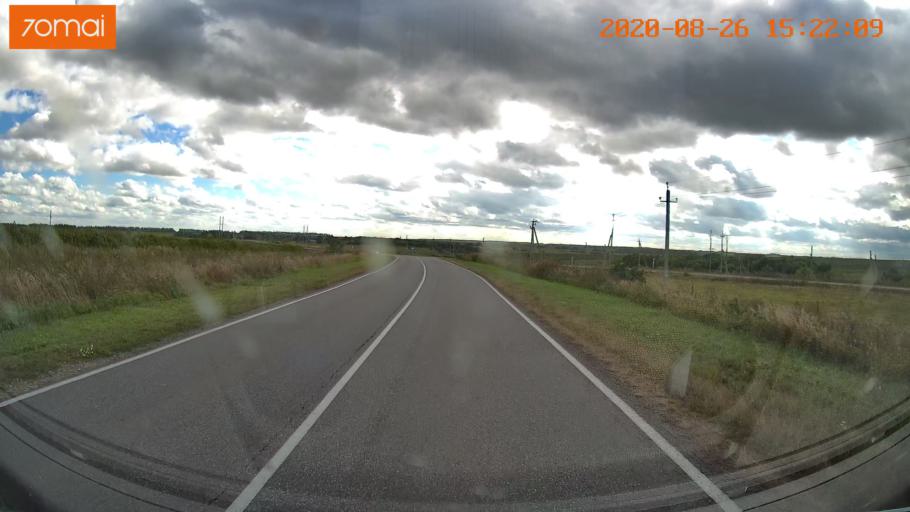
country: RU
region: Tula
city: Severo-Zadonsk
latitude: 54.1356
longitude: 38.4551
